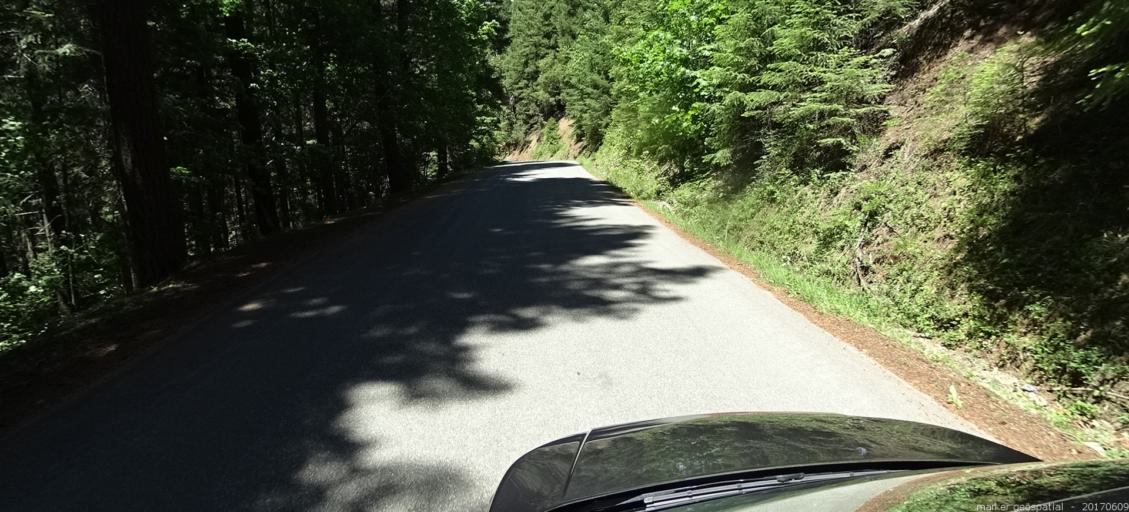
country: US
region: California
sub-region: Siskiyou County
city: Yreka
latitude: 41.3760
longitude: -123.0190
